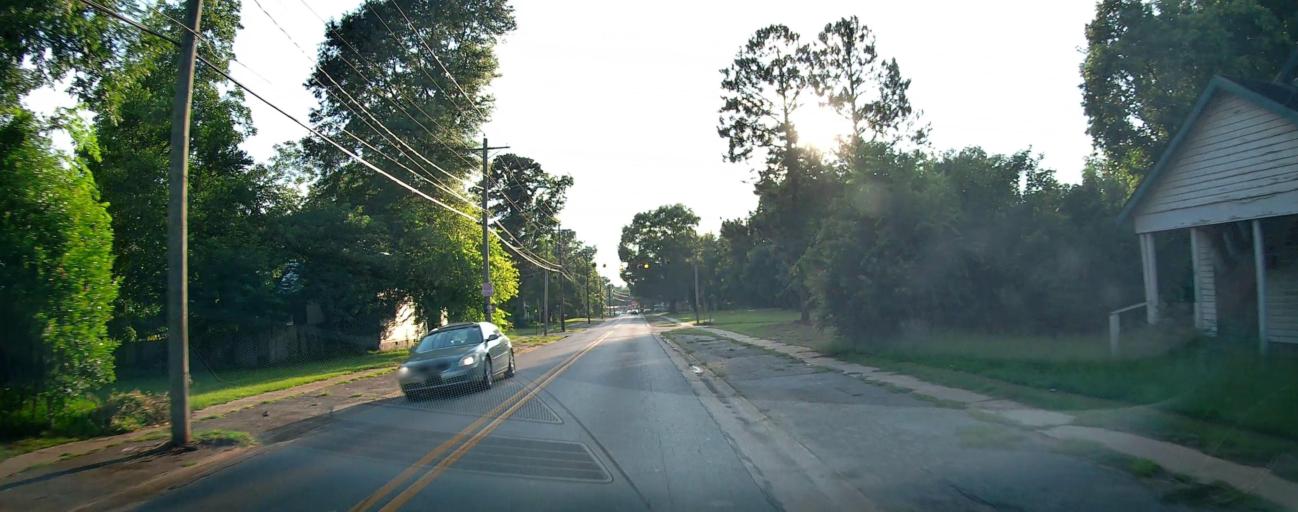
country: US
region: Georgia
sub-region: Peach County
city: Fort Valley
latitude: 32.5594
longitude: -83.8892
